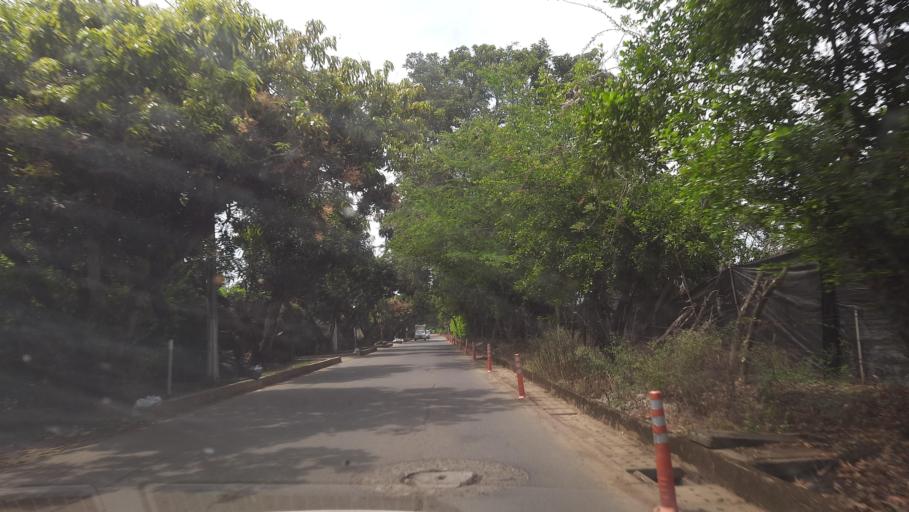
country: CO
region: Valle del Cauca
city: Jamundi
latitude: 3.2708
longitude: -76.5228
